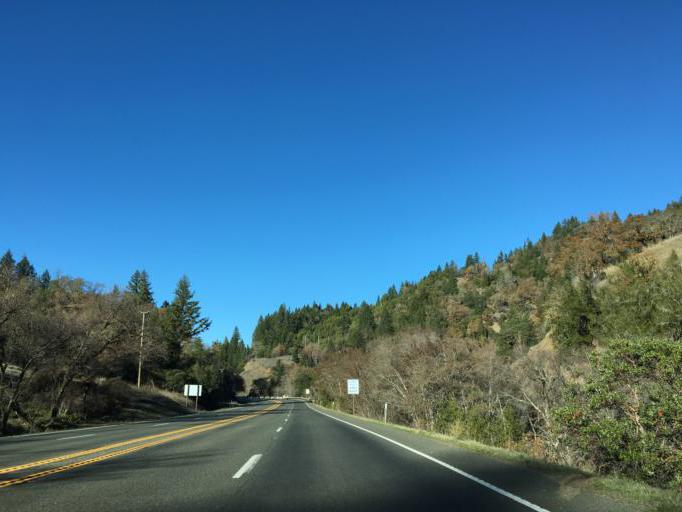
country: US
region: California
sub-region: Mendocino County
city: Brooktrails
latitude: 39.5604
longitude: -123.4328
